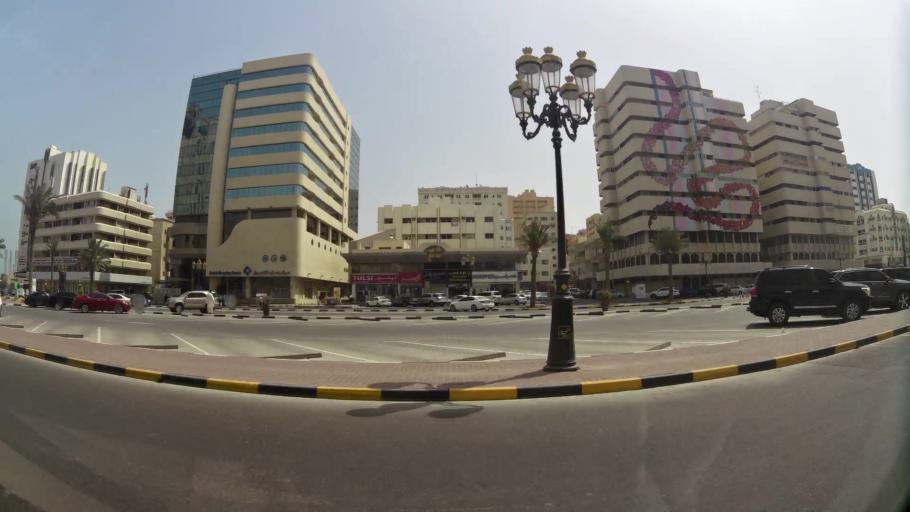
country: AE
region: Ash Shariqah
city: Sharjah
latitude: 25.3590
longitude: 55.3852
